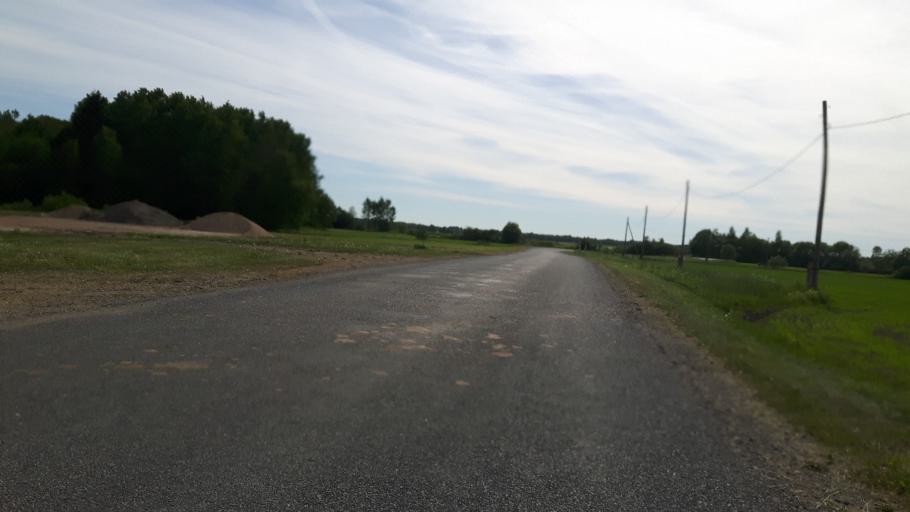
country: EE
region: Harju
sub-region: Raasiku vald
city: Arukula
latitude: 59.4237
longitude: 25.0858
